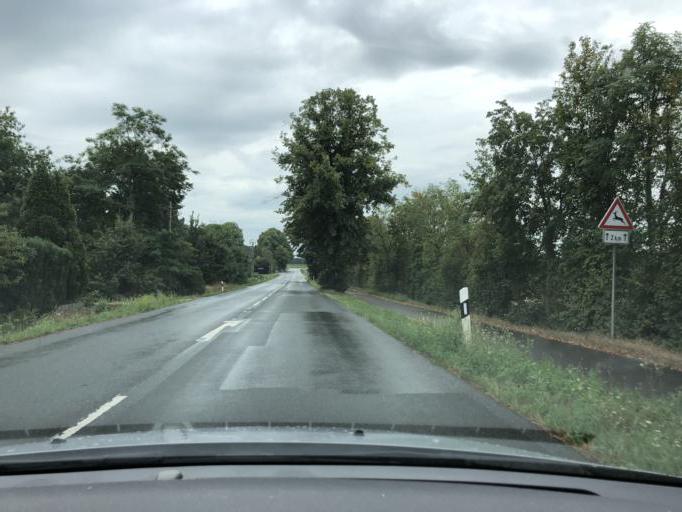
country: DE
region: North Rhine-Westphalia
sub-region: Regierungsbezirk Dusseldorf
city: Schermbeck
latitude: 51.7199
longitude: 6.8702
